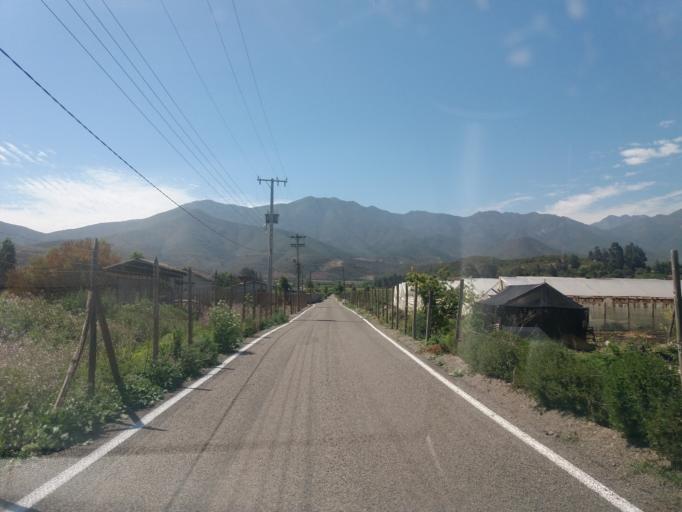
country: CL
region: Valparaiso
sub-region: Provincia de Quillota
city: Quillota
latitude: -32.8574
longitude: -71.2048
